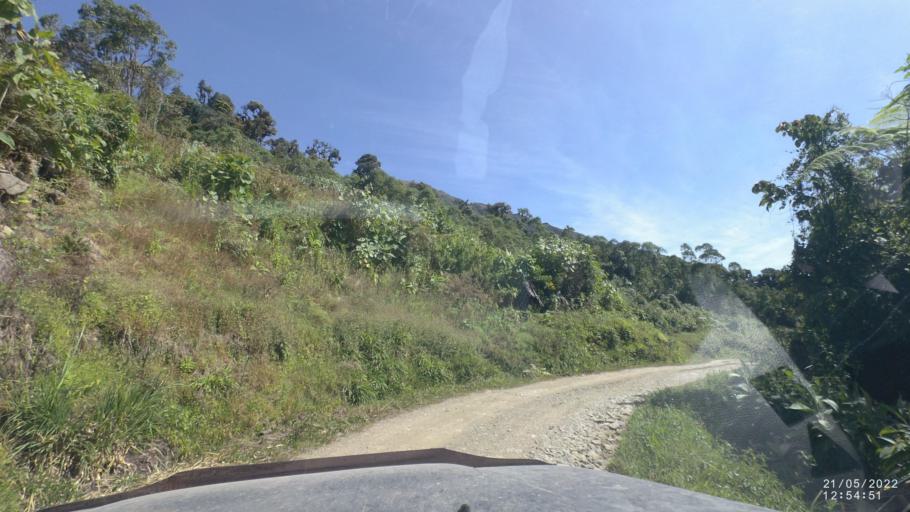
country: BO
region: Cochabamba
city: Colomi
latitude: -17.1771
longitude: -65.9424
